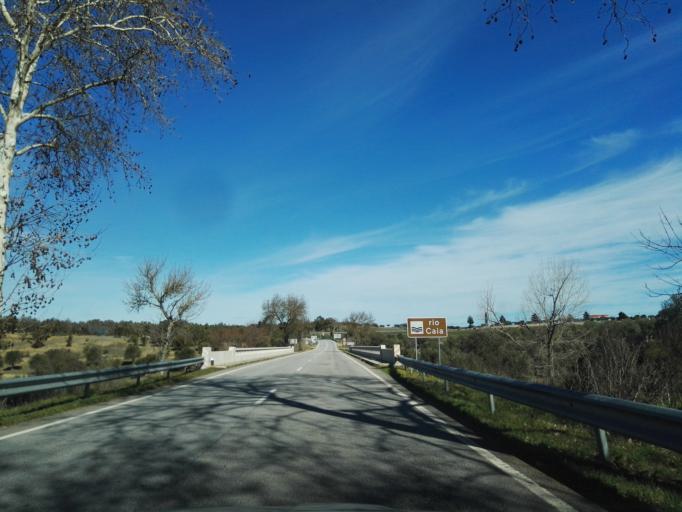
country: PT
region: Portalegre
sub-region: Arronches
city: Arronches
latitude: 39.1306
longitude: -7.2930
